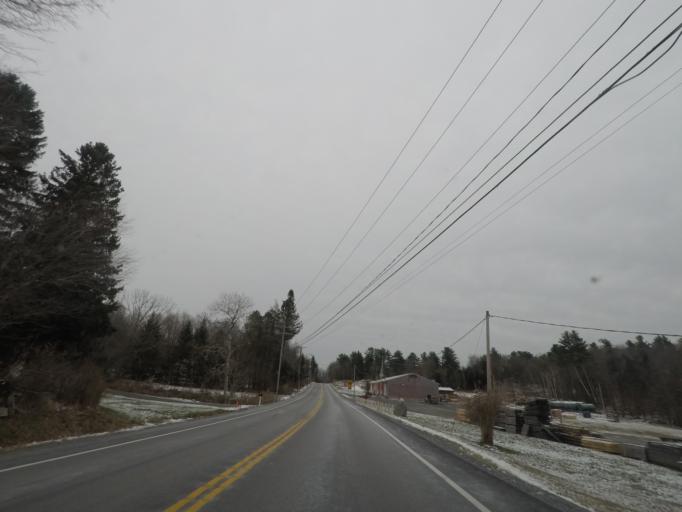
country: US
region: New York
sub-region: Rensselaer County
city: Hoosick Falls
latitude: 42.7689
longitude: -73.4190
